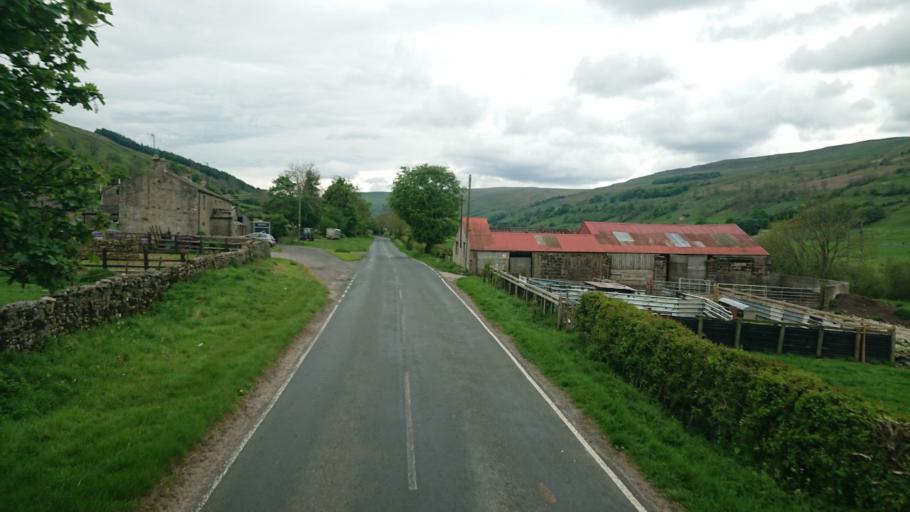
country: GB
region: England
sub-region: North Yorkshire
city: Leyburn
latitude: 54.2600
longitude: -2.0253
